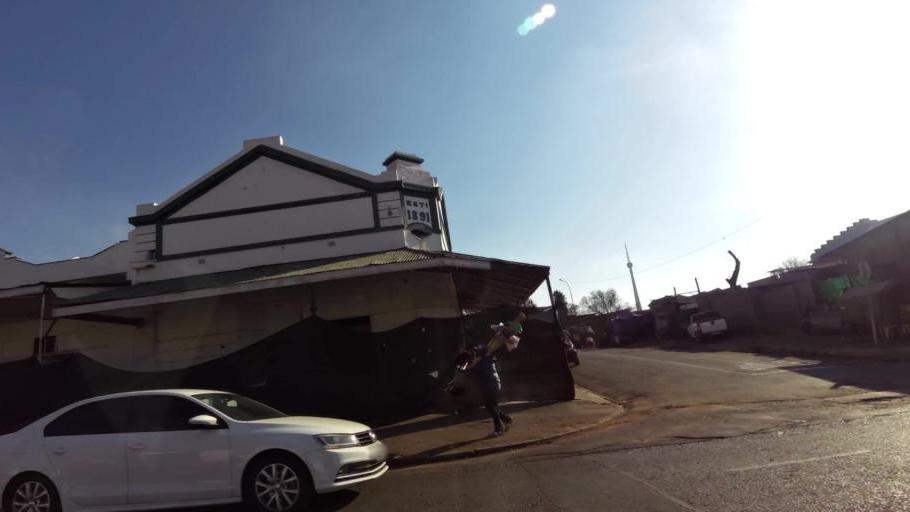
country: ZA
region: Gauteng
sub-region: City of Johannesburg Metropolitan Municipality
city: Johannesburg
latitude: -26.1954
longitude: 28.0206
